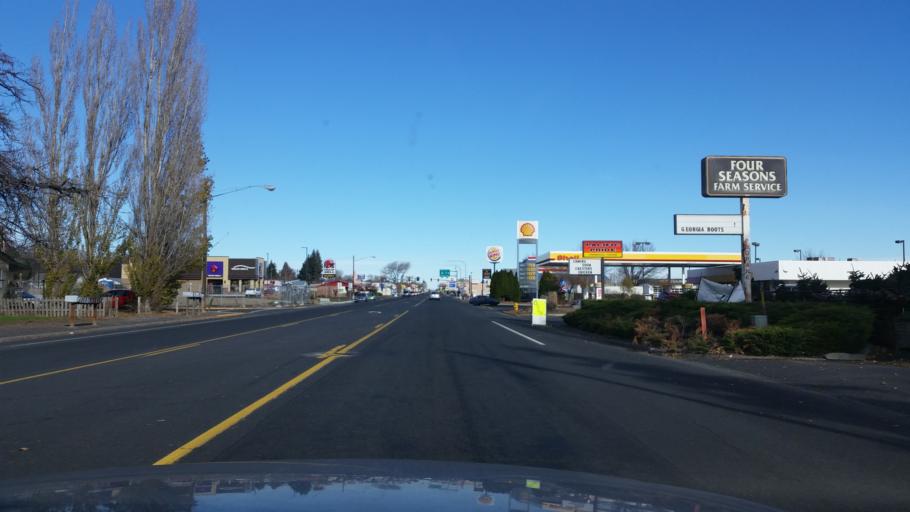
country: US
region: Washington
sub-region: Grant County
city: Ephrata
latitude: 47.3063
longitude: -119.5620
